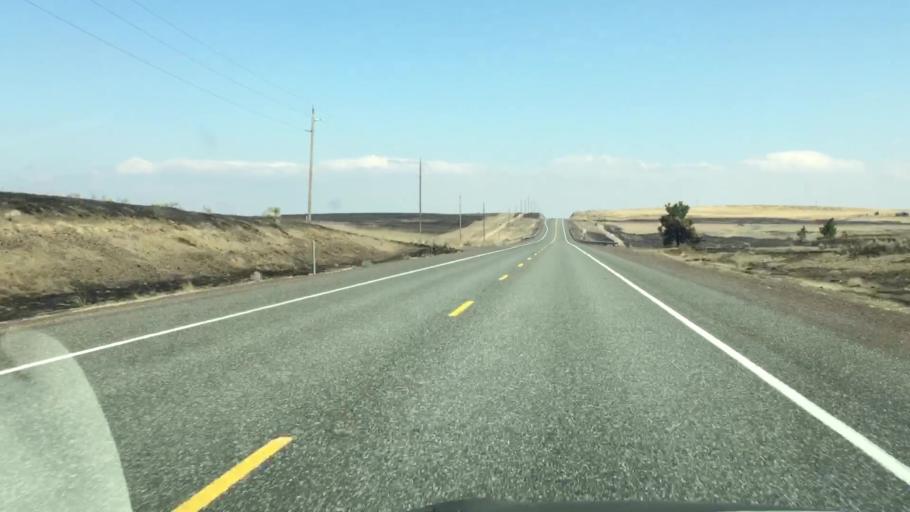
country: US
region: Oregon
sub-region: Wasco County
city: The Dalles
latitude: 45.3508
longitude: -121.1422
